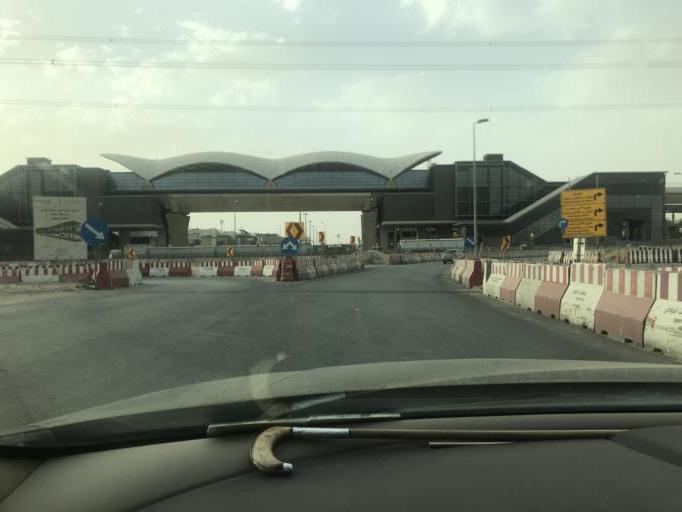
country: SA
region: Ar Riyad
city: Riyadh
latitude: 24.7851
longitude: 46.6608
